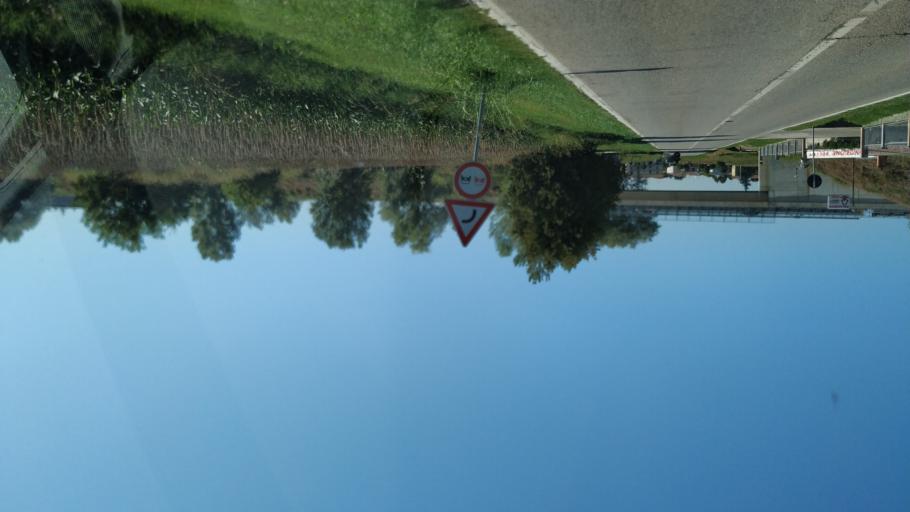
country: IT
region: Emilia-Romagna
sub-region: Provincia di Ferrara
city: San Carlo
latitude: 44.7986
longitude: 11.4035
